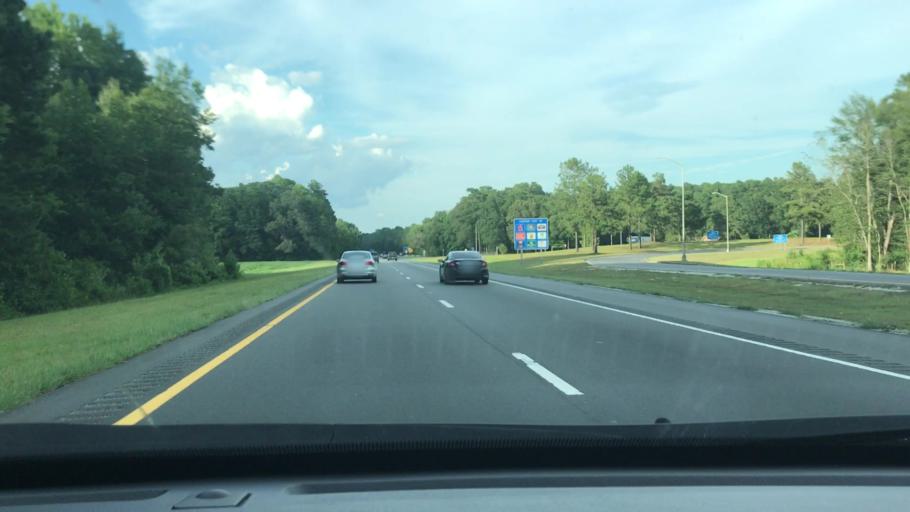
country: US
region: North Carolina
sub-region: Cumberland County
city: Vander
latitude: 34.9952
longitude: -78.8313
